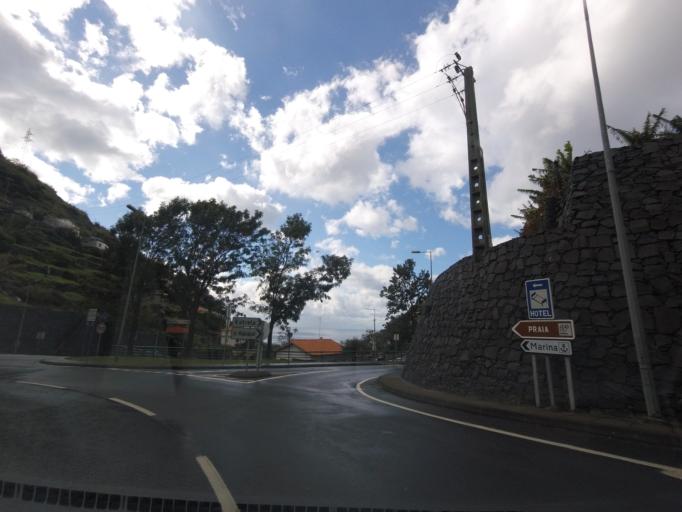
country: PT
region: Madeira
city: Calheta
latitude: 32.7261
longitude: -17.1733
